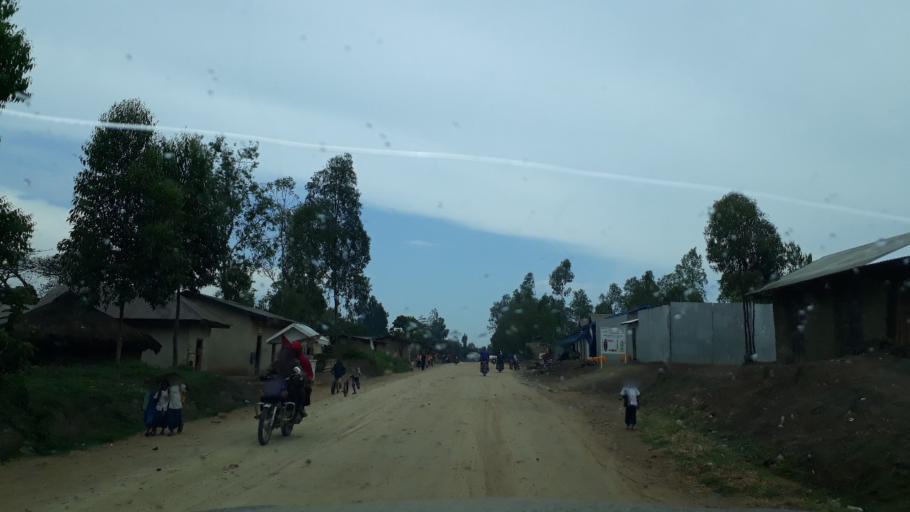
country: CD
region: Eastern Province
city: Bunia
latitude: 1.5947
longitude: 30.2615
